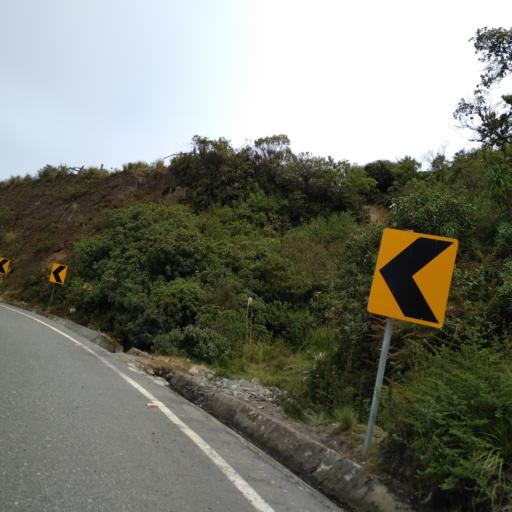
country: EC
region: Cotopaxi
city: La Mana
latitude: -0.9870
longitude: -78.9703
